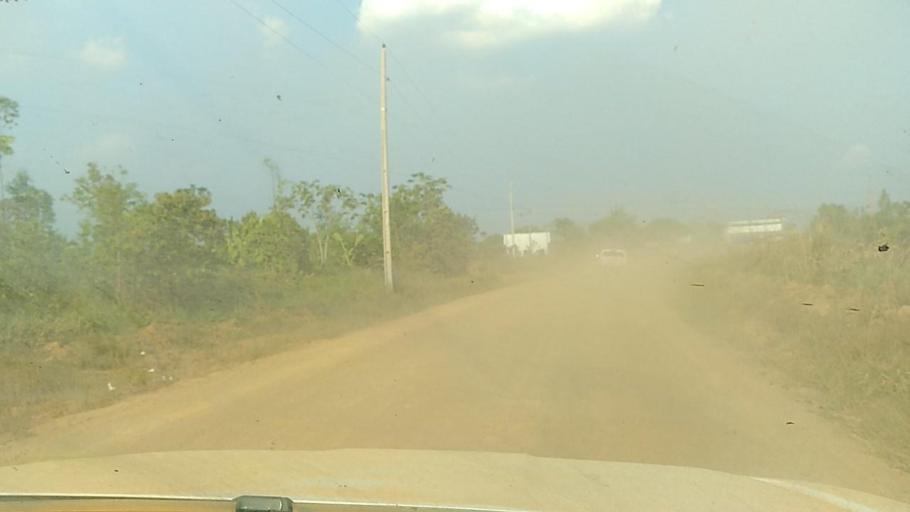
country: BR
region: Rondonia
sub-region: Porto Velho
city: Porto Velho
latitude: -8.6705
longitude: -63.9954
